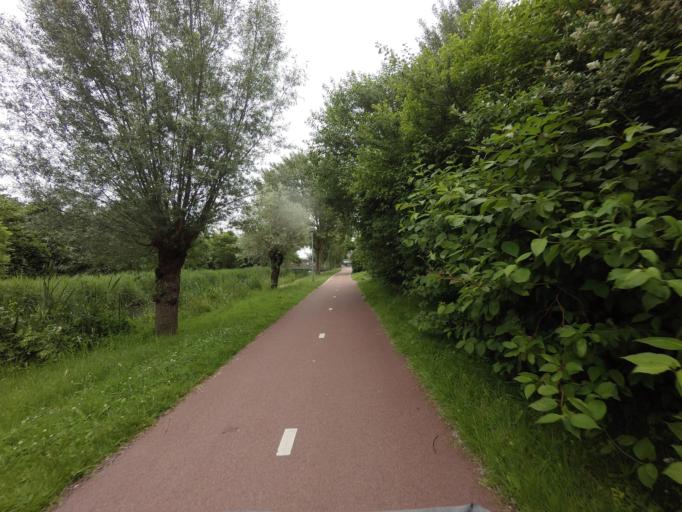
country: NL
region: North Holland
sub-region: Gemeente Huizen
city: Huizen
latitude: 52.2983
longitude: 5.2780
